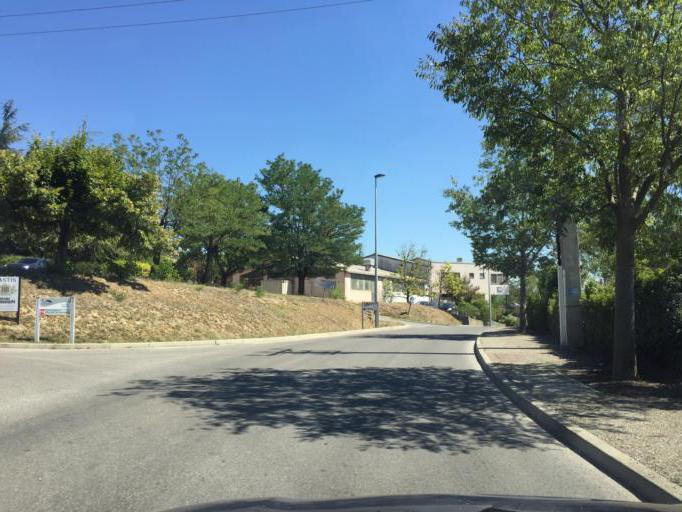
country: FR
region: Provence-Alpes-Cote d'Azur
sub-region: Departement des Alpes-de-Haute-Provence
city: Forcalquier
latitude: 43.9577
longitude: 5.7968
